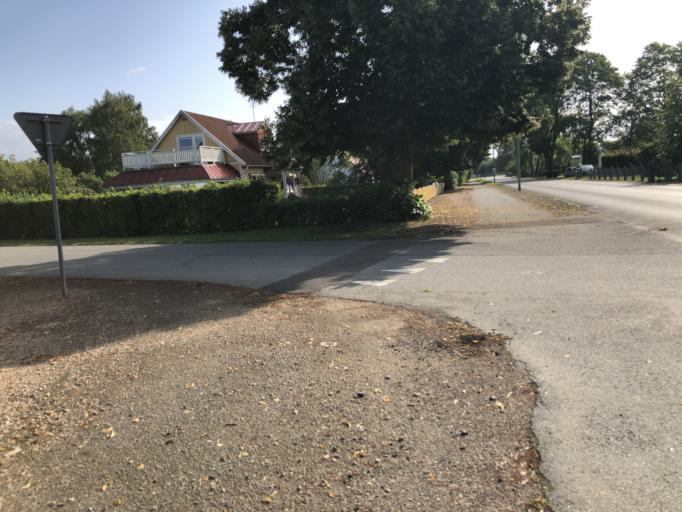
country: SE
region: Skane
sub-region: Hassleholms Kommun
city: Vinslov
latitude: 56.1045
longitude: 13.9244
